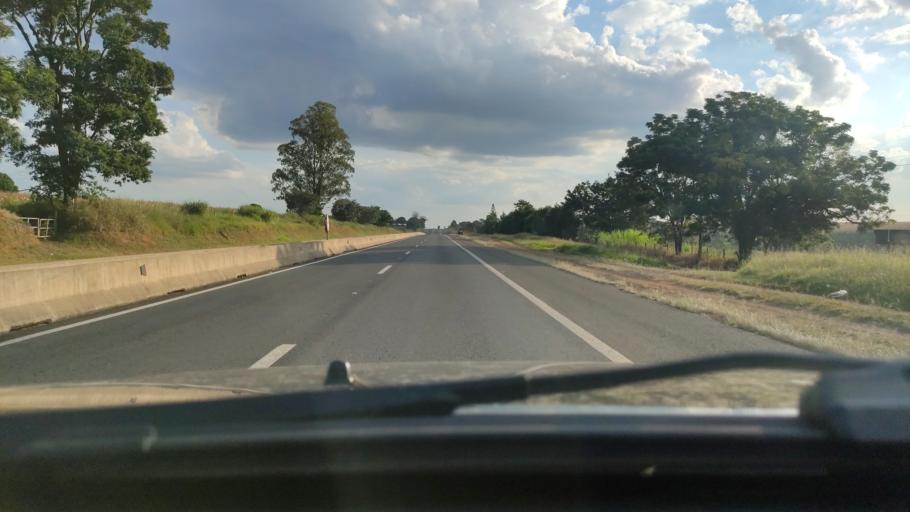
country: BR
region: Sao Paulo
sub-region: Artur Nogueira
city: Artur Nogueira
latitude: -22.4612
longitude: -47.1012
